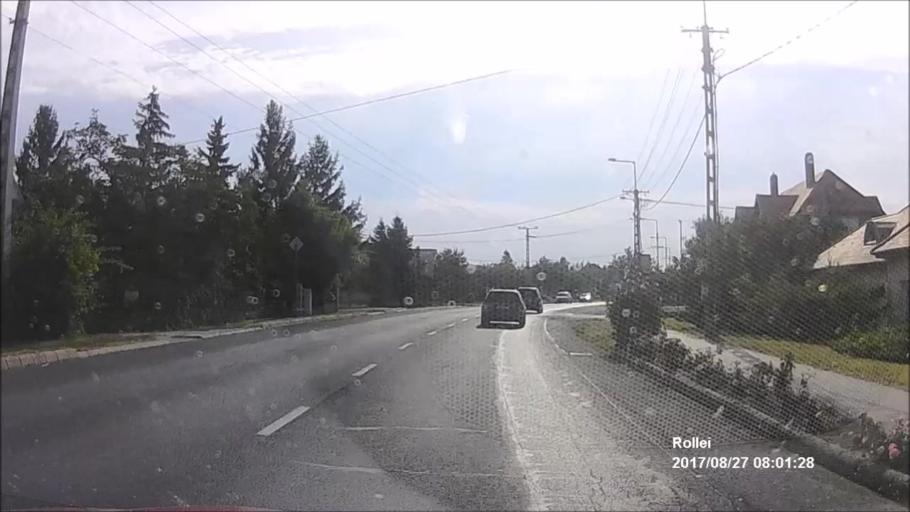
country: HU
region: Zala
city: Vonyarcvashegy
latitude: 46.7628
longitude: 17.3121
